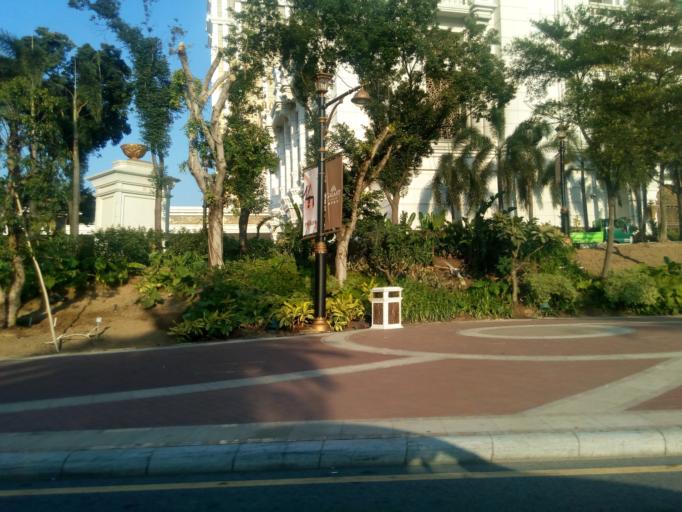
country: MO
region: Macau
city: Macau
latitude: 22.1496
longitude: 113.5513
